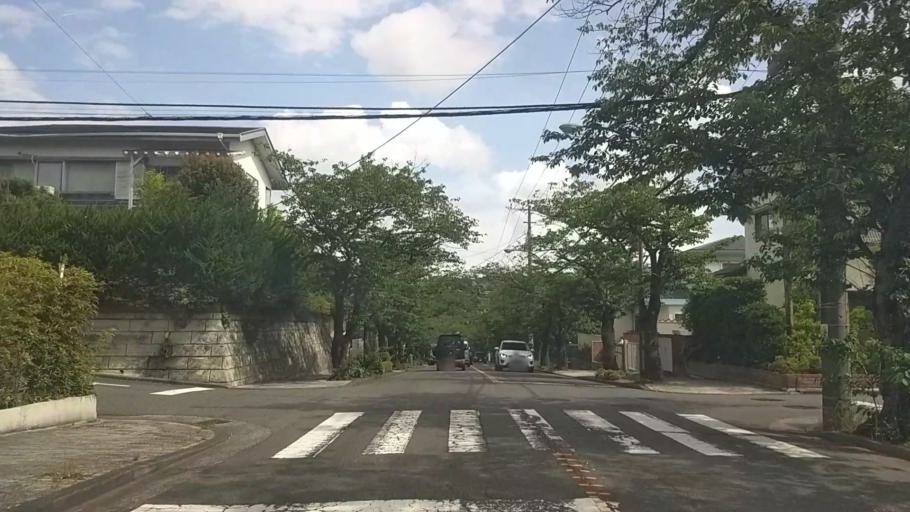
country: JP
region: Kanagawa
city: Zushi
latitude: 35.3150
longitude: 139.5768
